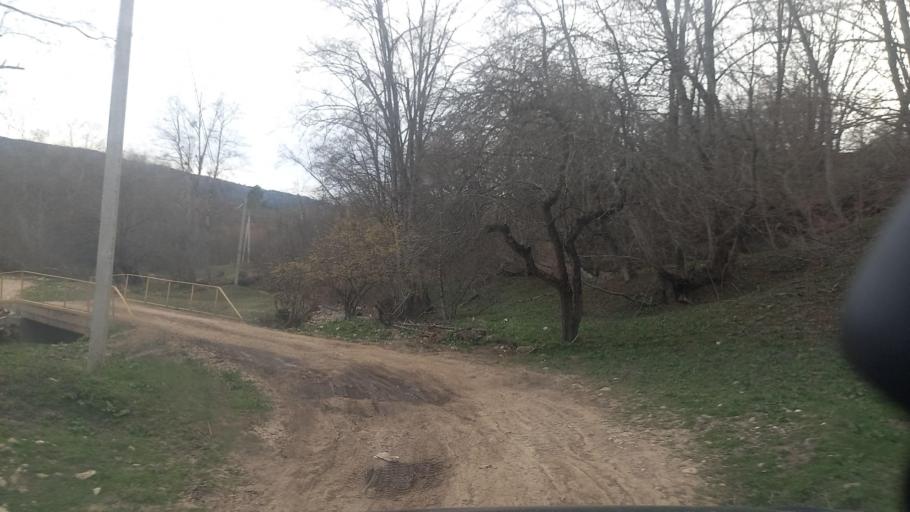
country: RU
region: Adygeya
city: Kamennomostskiy
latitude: 44.2143
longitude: 40.0196
